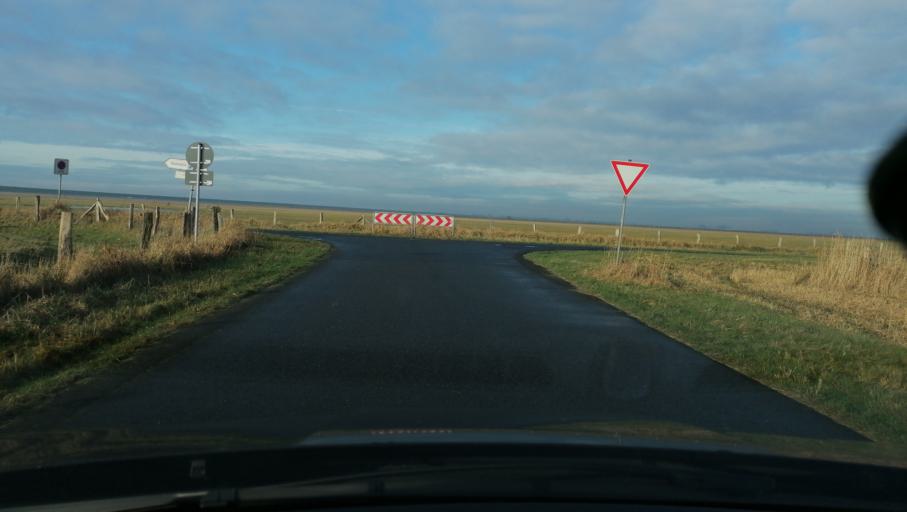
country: DE
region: Schleswig-Holstein
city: Friedrichsgabekoog
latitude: 54.1120
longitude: 8.9517
